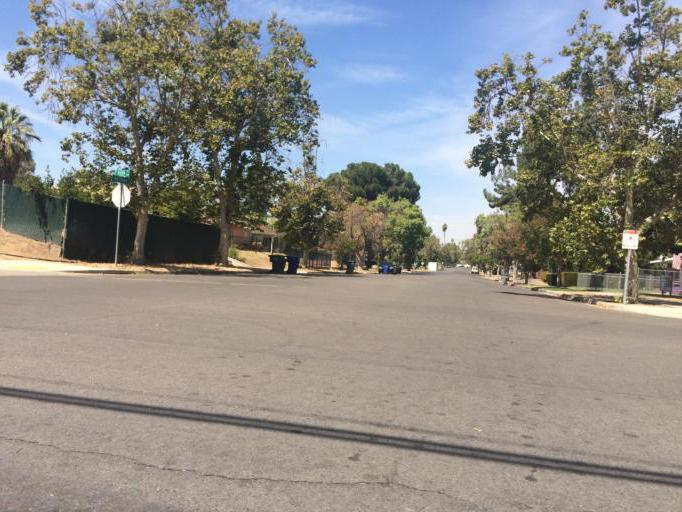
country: US
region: California
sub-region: Fresno County
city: Fresno
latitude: 36.7229
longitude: -119.8029
